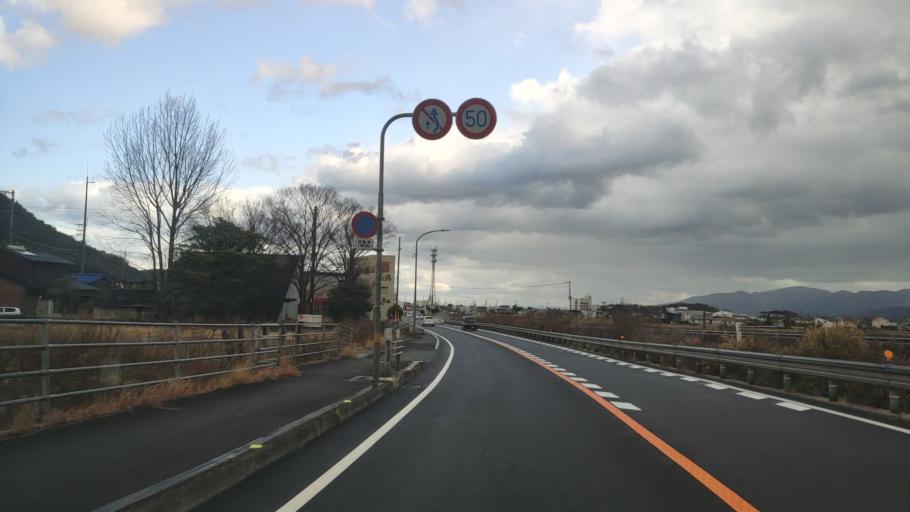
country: JP
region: Tokushima
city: Kamojimacho-jogejima
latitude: 34.2234
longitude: 134.3928
